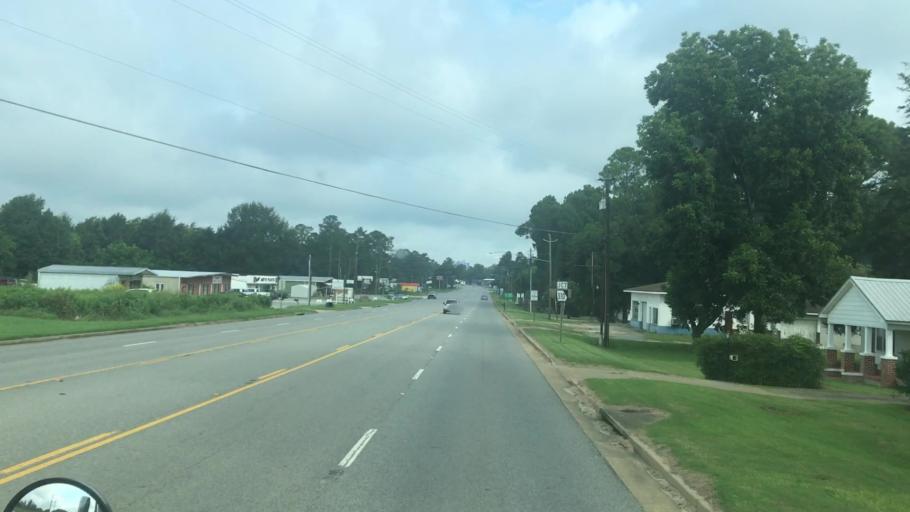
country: US
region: Georgia
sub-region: Miller County
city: Colquitt
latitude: 31.1638
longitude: -84.7212
